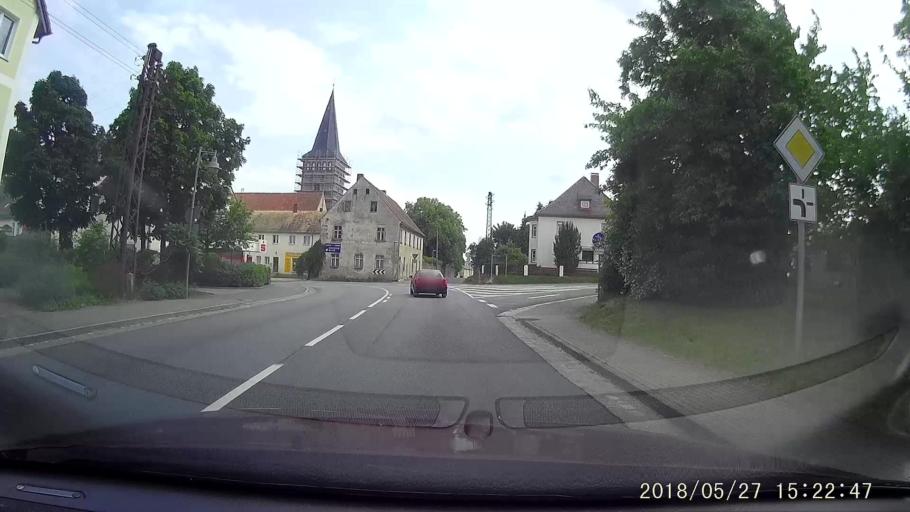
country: DE
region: Saxony
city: Kodersdorf
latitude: 51.2309
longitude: 14.8923
